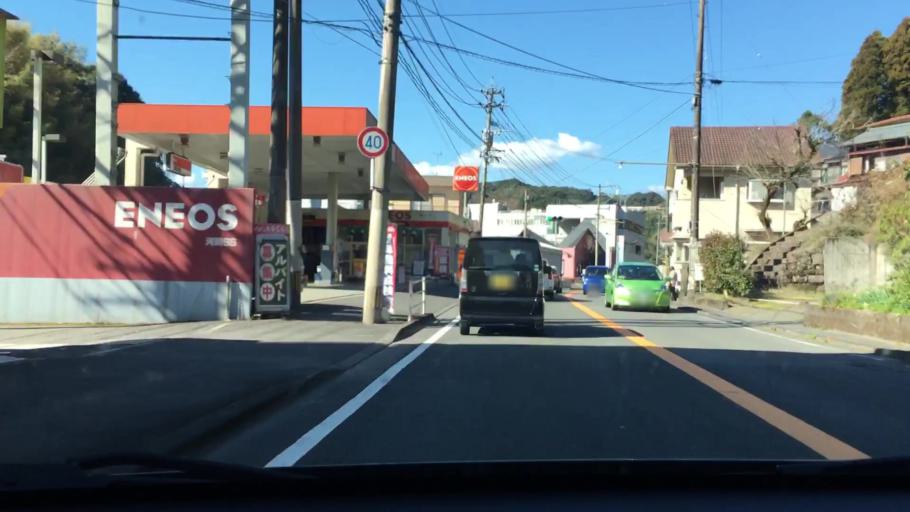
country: JP
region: Kagoshima
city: Kagoshima-shi
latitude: 31.6396
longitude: 130.5173
